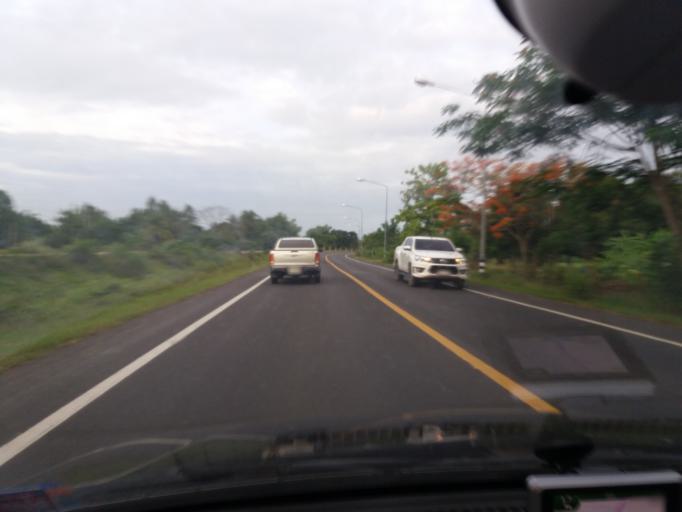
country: TH
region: Suphan Buri
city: Don Chedi
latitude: 14.5229
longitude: 99.9269
